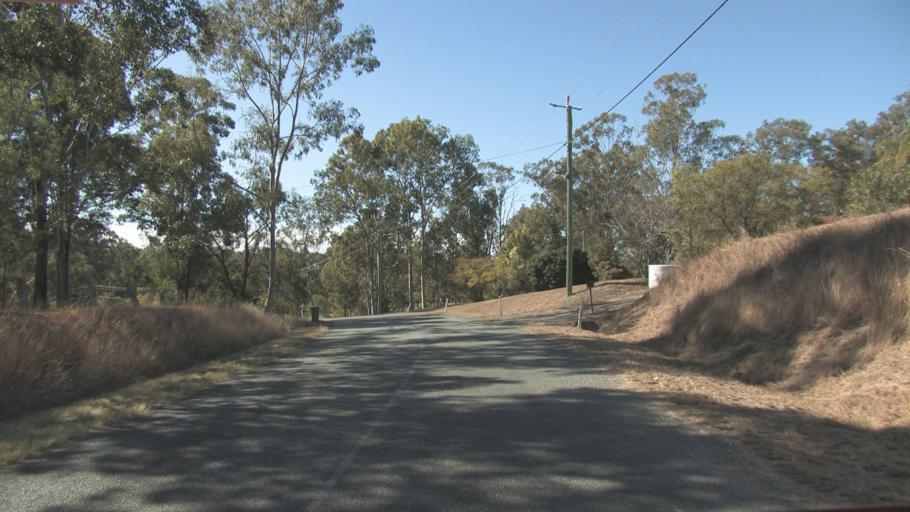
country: AU
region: Queensland
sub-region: Logan
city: Cedar Vale
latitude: -27.8865
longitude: 152.9988
